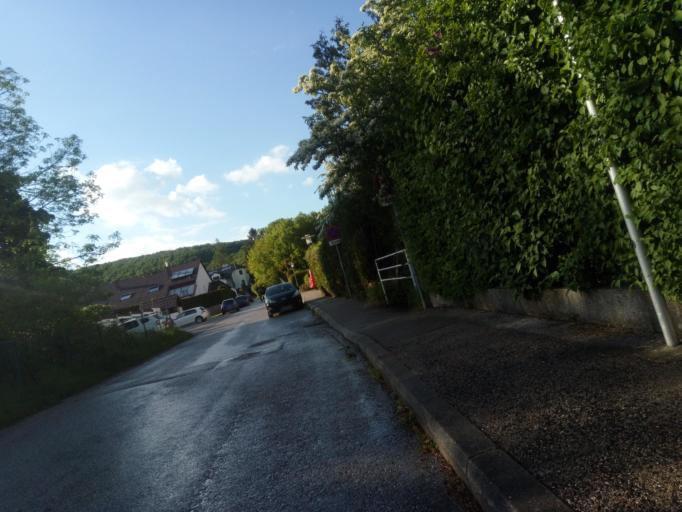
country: AT
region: Lower Austria
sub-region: Politischer Bezirk Modling
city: Kaltenleutgeben
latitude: 48.1365
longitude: 16.1911
